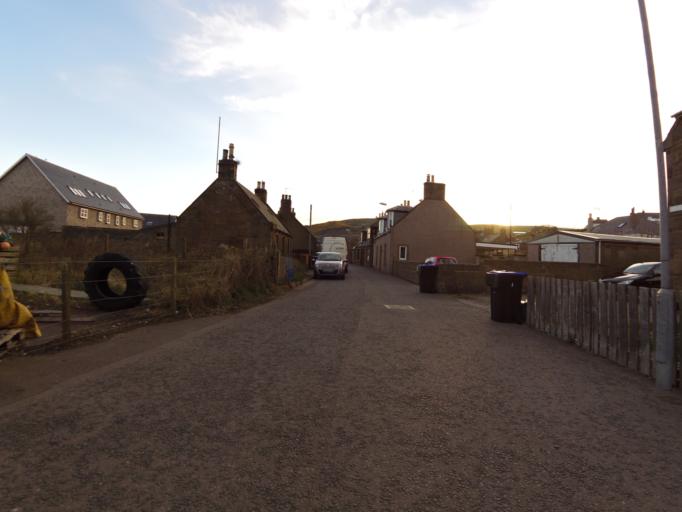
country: GB
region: Scotland
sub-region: Aberdeenshire
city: Inverbervie
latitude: 56.8290
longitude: -2.2808
